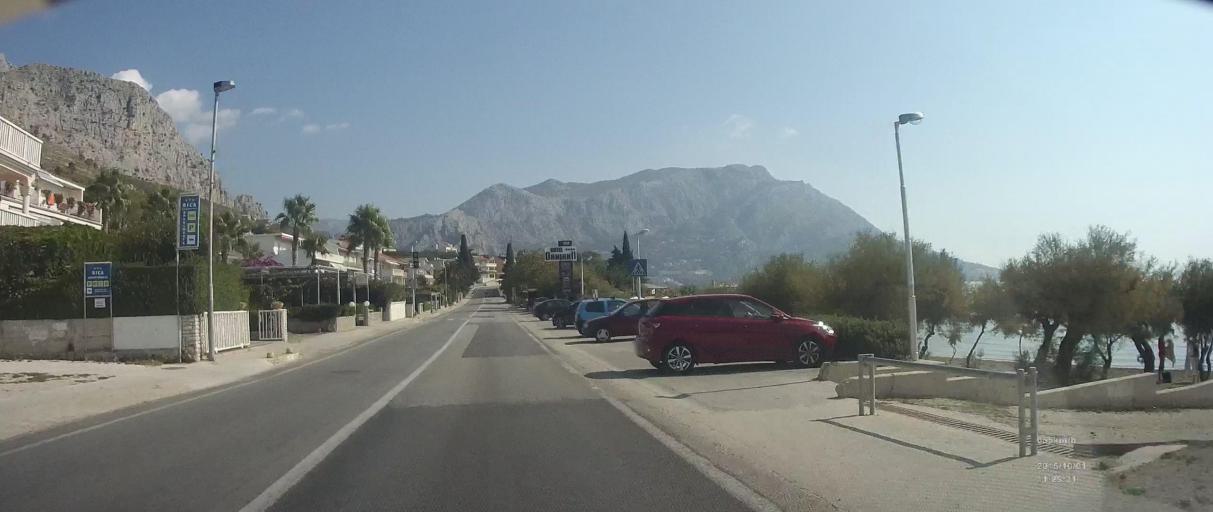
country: HR
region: Splitsko-Dalmatinska
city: Duce
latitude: 43.4394
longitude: 16.6671
